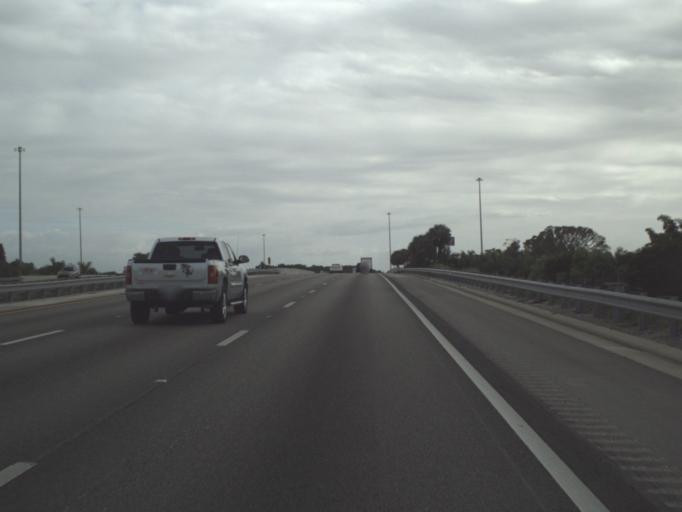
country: US
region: Florida
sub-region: Lee County
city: Tice
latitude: 26.6858
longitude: -81.7989
